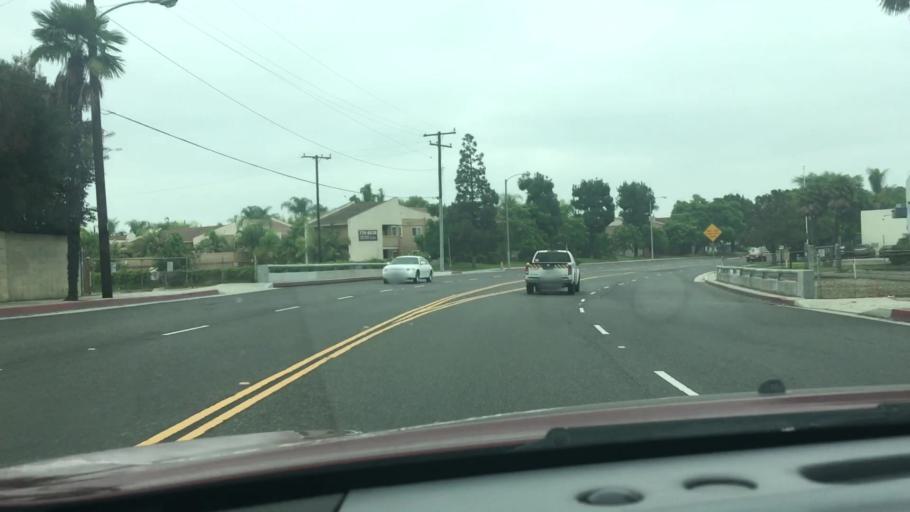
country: US
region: California
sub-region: Orange County
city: Buena Park
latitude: 33.8831
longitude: -118.0008
